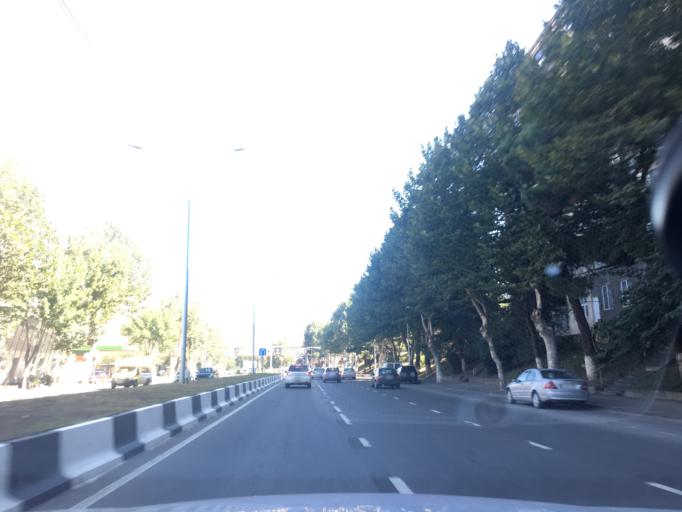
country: GE
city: Zahesi
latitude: 41.7815
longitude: 44.7977
